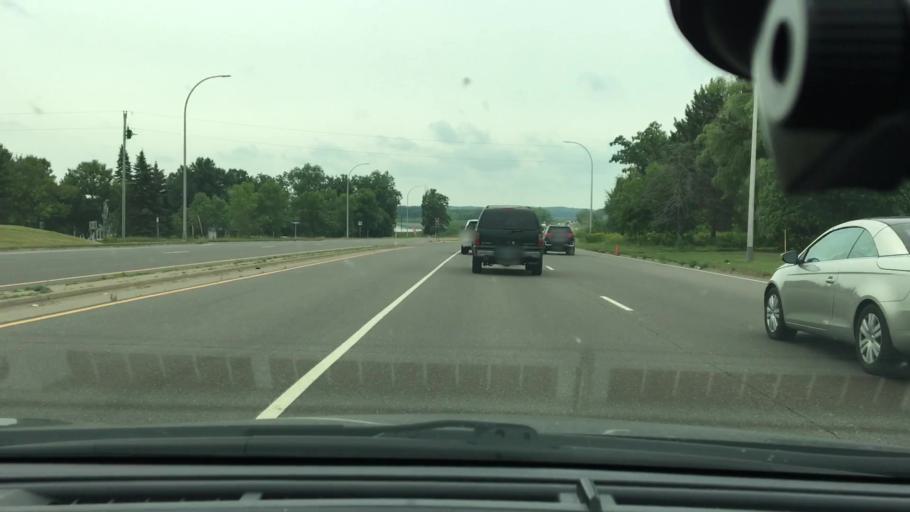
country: US
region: Minnesota
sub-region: Mille Lacs County
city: Vineland
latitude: 46.1779
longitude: -93.7567
